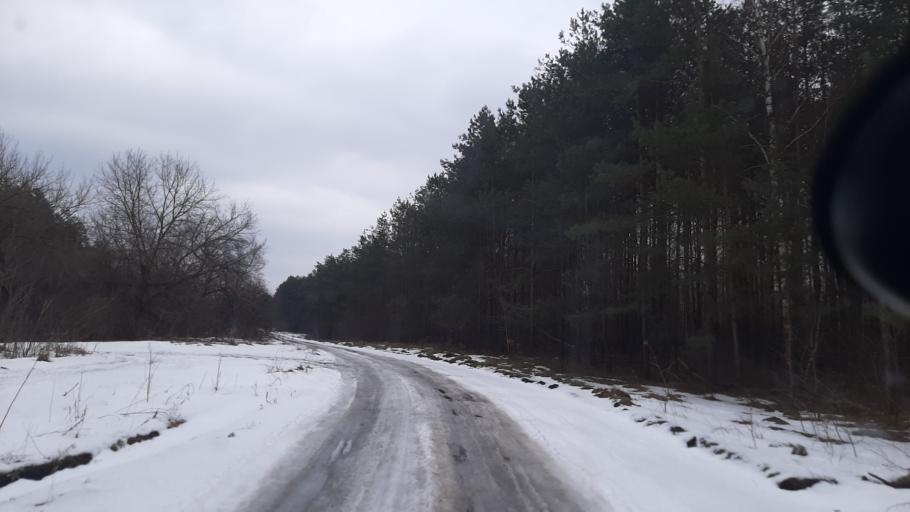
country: PL
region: Lublin Voivodeship
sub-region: Powiat wlodawski
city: Wlodawa
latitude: 51.5179
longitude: 23.5927
